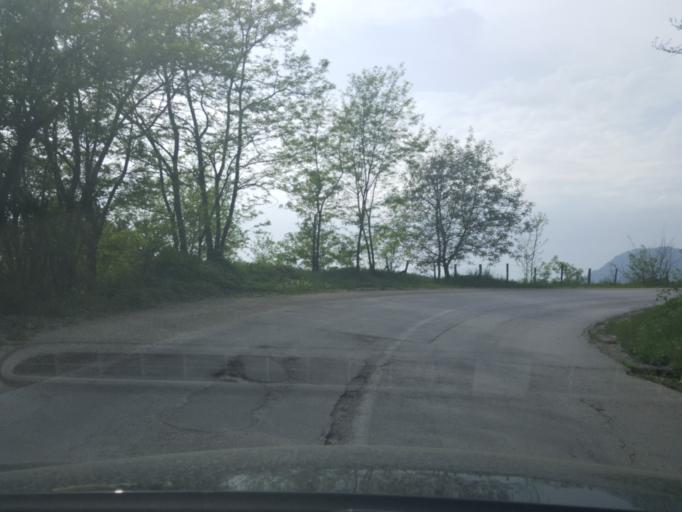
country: RS
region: Central Serbia
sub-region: Zlatiborski Okrug
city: Bajina Basta
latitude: 44.0756
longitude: 19.6628
